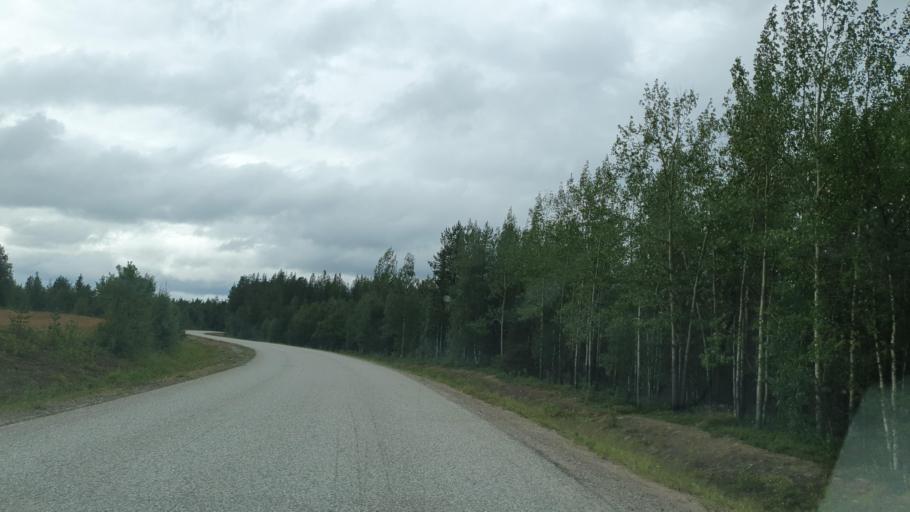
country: FI
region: Lapland
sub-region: Tunturi-Lappi
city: Kolari
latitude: 67.5037
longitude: 24.2695
